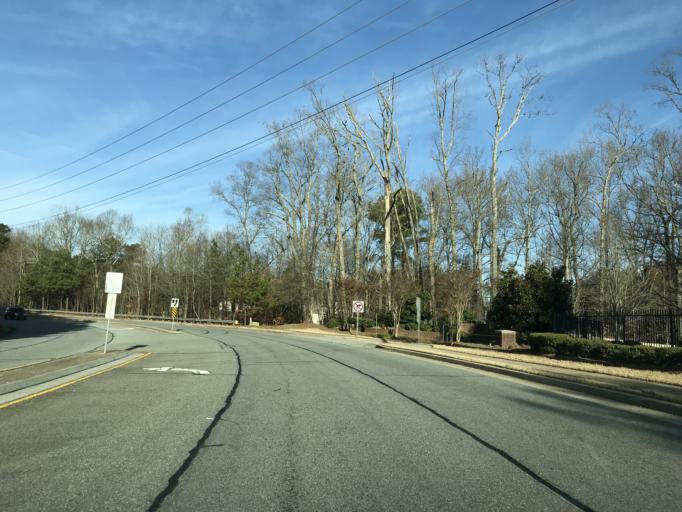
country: US
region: Georgia
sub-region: Cobb County
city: Kennesaw
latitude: 34.0545
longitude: -84.5875
